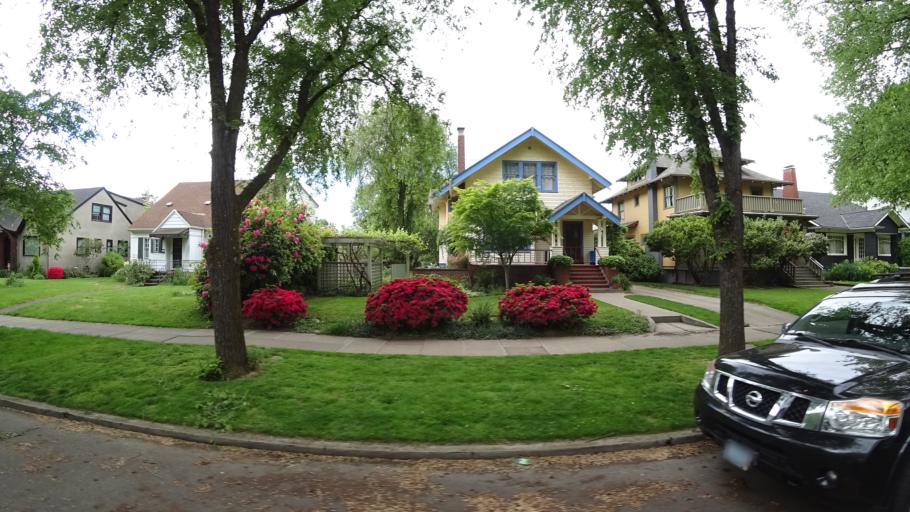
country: US
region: Oregon
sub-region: Multnomah County
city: Portland
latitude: 45.5077
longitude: -122.6505
